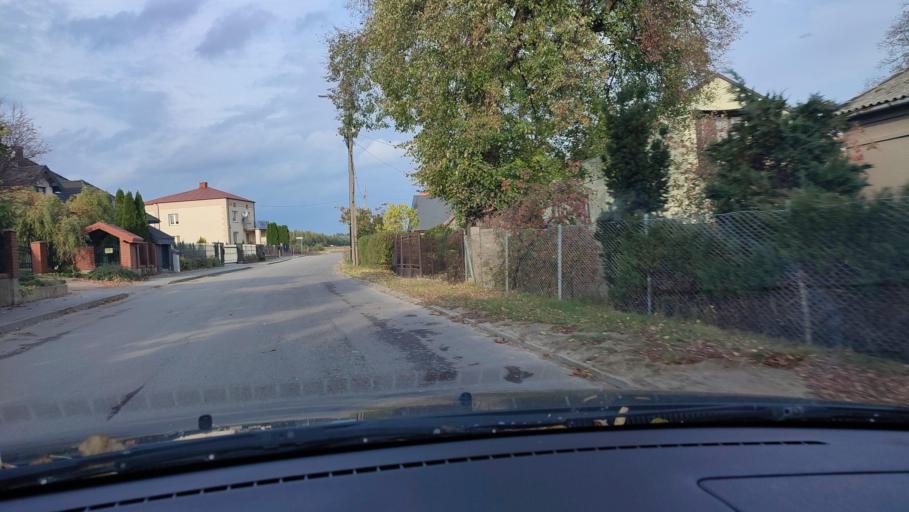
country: PL
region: Masovian Voivodeship
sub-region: Powiat mlawski
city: Mlawa
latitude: 53.1372
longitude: 20.3653
